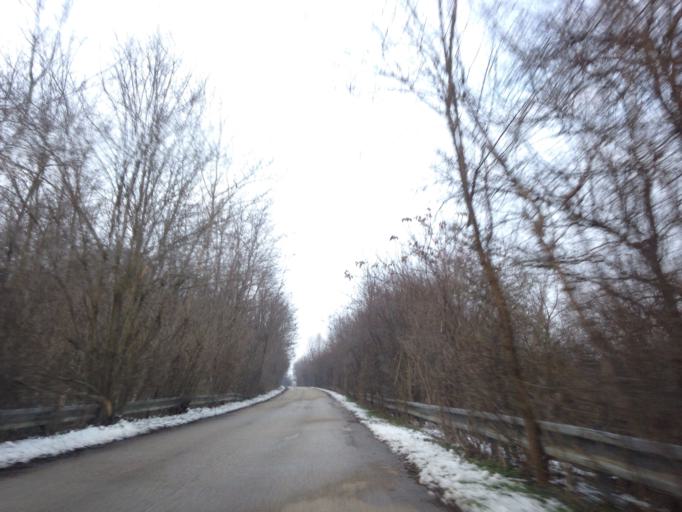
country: SK
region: Nitriansky
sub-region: Okres Nitra
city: Vrable
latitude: 48.0760
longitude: 18.3718
